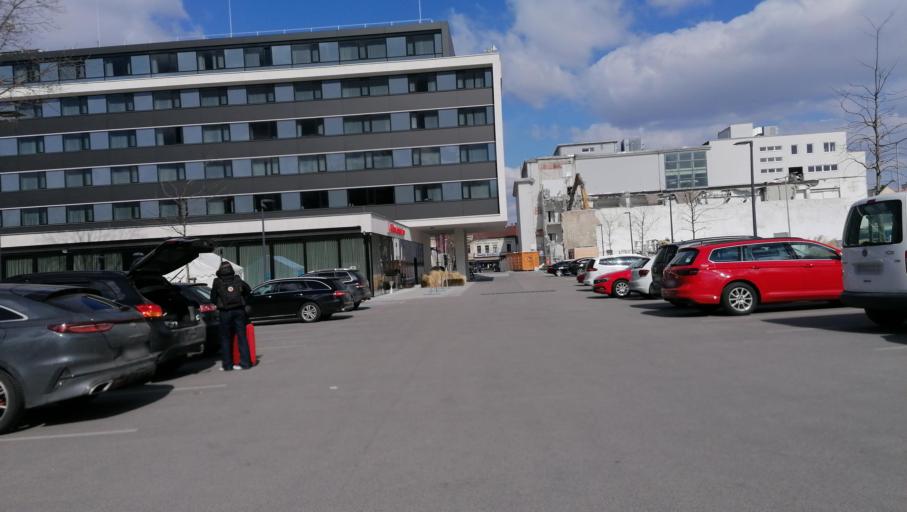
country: AT
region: Lower Austria
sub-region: Wiener Neustadt Stadt
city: Wiener Neustadt
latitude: 47.8096
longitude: 16.2405
